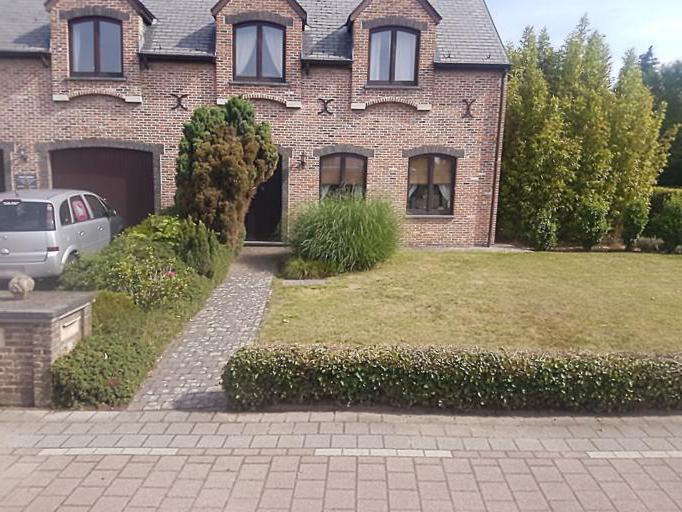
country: BE
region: Flanders
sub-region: Provincie Antwerpen
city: Berlaar
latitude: 51.1191
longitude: 4.6389
